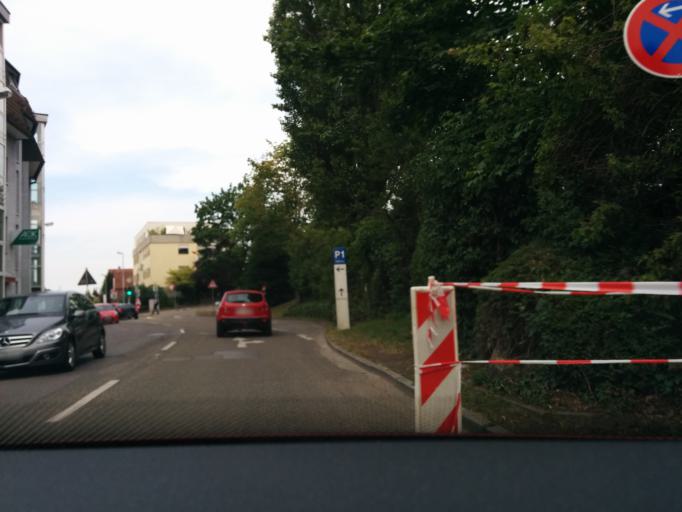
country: DE
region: Baden-Wuerttemberg
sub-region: Regierungsbezirk Stuttgart
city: Ditzingen
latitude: 48.8242
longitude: 9.0668
